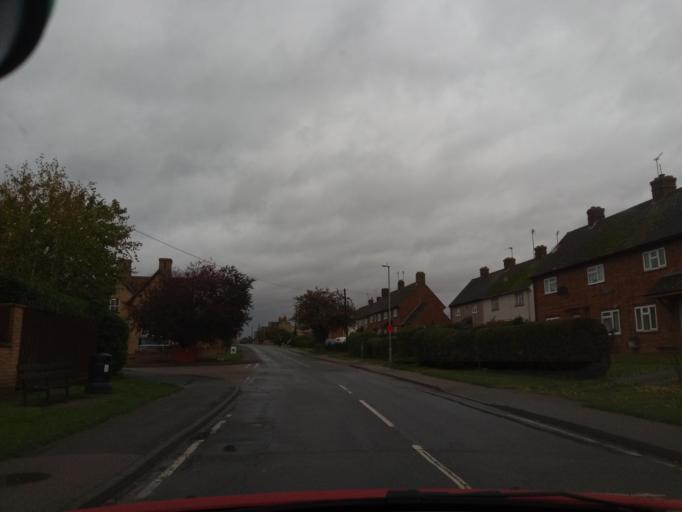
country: GB
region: England
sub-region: Cambridgeshire
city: Sawtry
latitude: 52.4344
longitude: -0.2811
